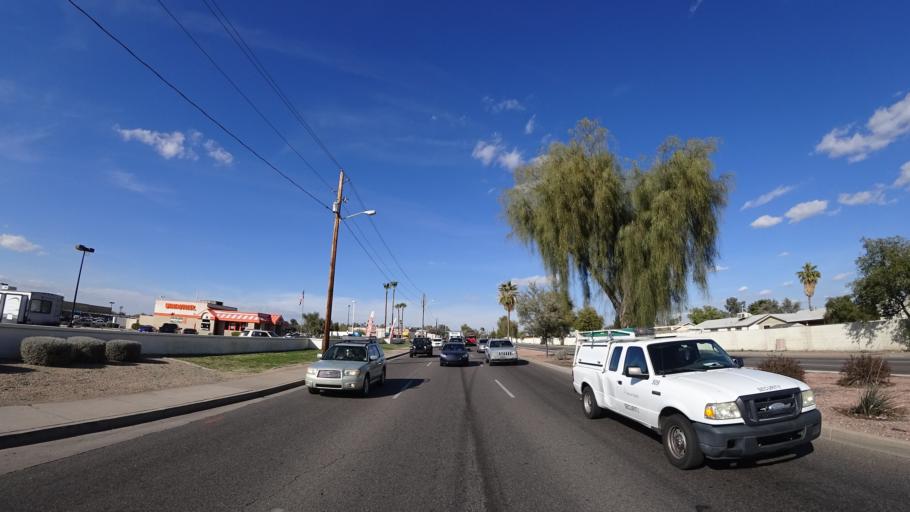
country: US
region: Arizona
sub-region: Maricopa County
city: Tolleson
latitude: 33.4702
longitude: -112.2208
